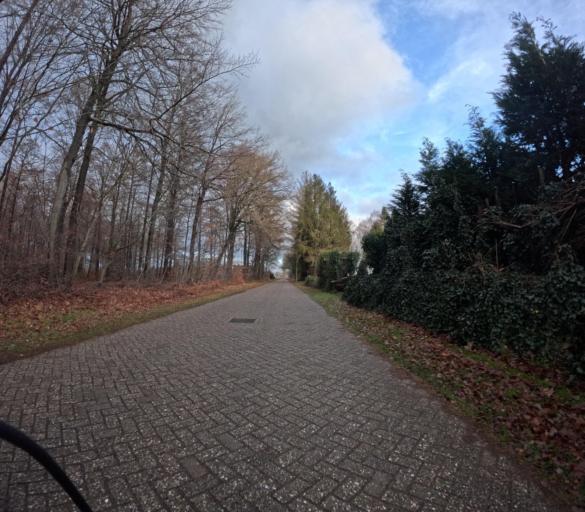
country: NL
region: Drenthe
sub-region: Gemeente Emmen
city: Emmen
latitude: 52.8031
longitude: 6.9135
